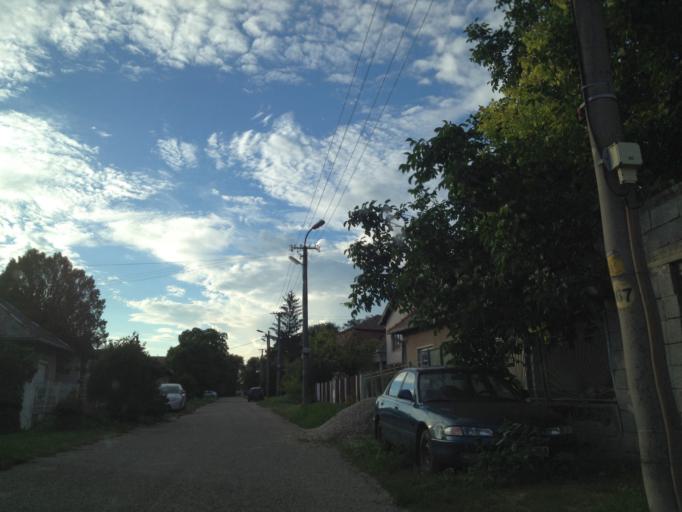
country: SK
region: Nitriansky
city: Svodin
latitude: 47.9027
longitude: 18.4222
